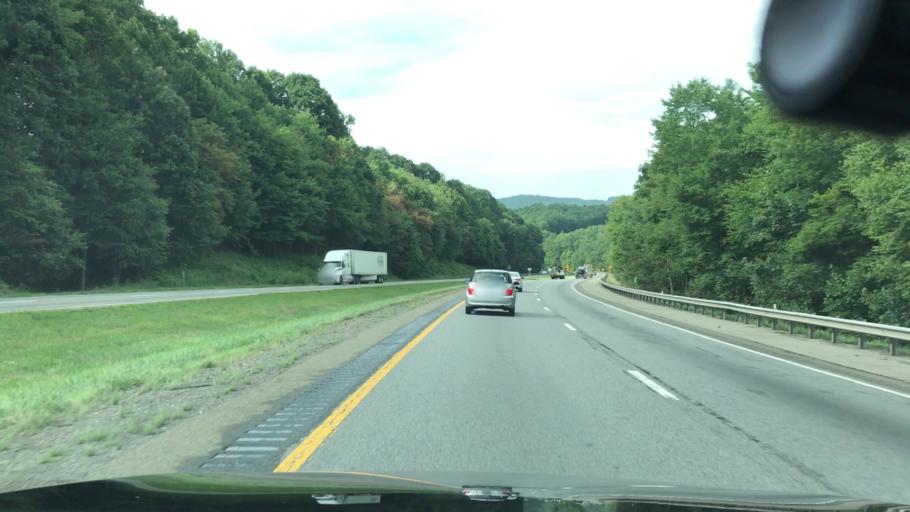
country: US
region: Virginia
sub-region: Carroll County
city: Woodlawn
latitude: 36.8139
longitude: -80.8543
